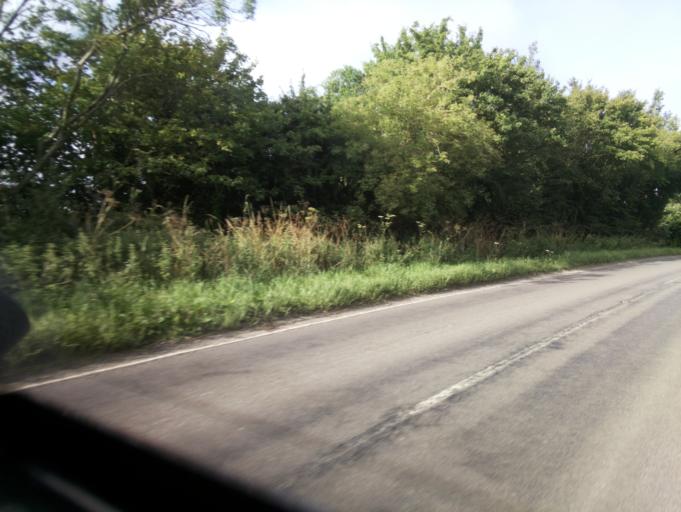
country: GB
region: England
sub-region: Borough of Swindon
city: Hannington
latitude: 51.6202
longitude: -1.7500
